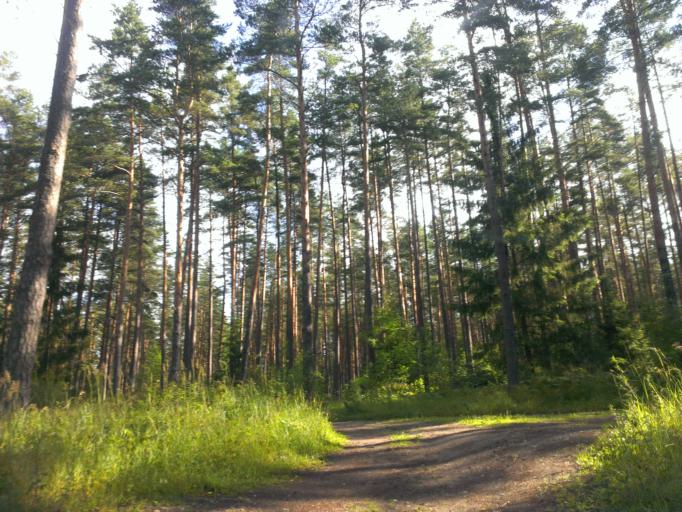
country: LV
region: Incukalns
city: Vangazi
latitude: 57.0997
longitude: 24.5378
